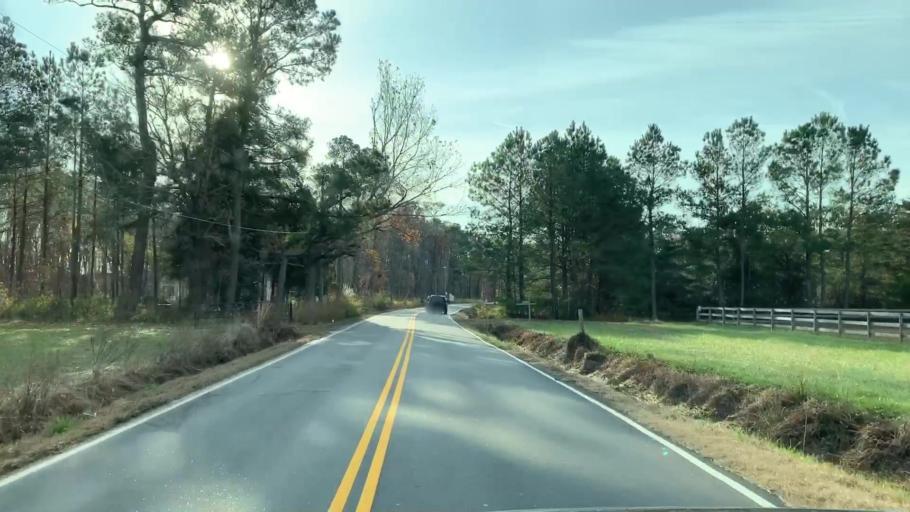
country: US
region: Virginia
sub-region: City of Virginia Beach
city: Virginia Beach
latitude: 36.7134
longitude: -76.0492
